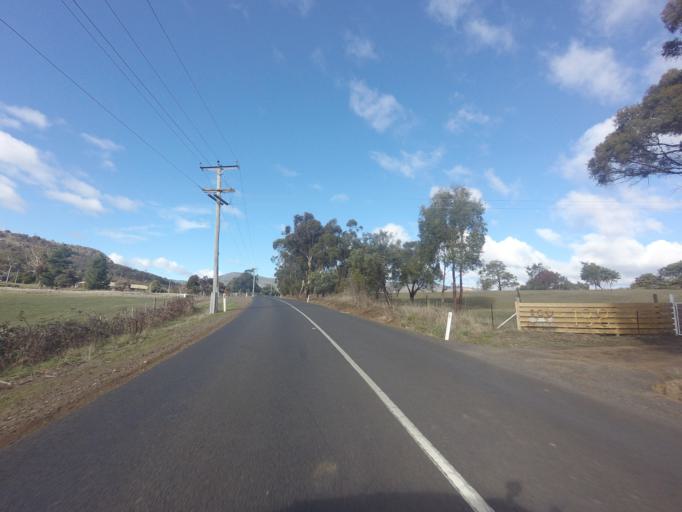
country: AU
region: Tasmania
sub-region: Derwent Valley
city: New Norfolk
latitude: -42.7889
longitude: 147.1210
